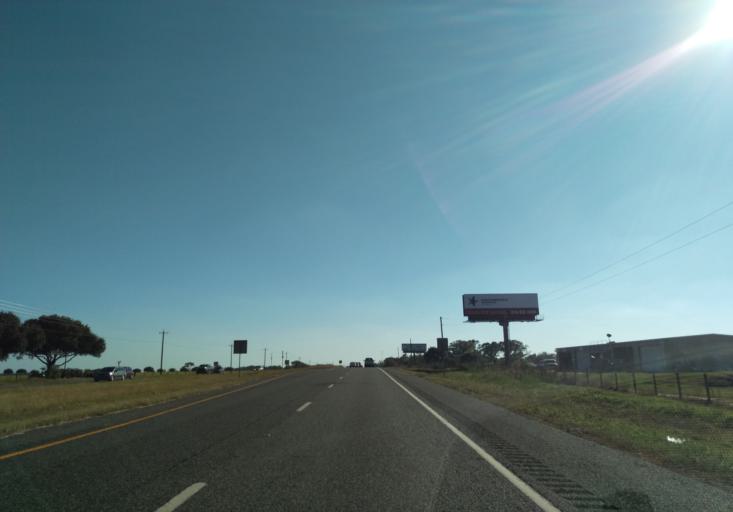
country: US
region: Texas
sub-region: Waller County
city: Hempstead
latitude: 30.1535
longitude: -96.0691
